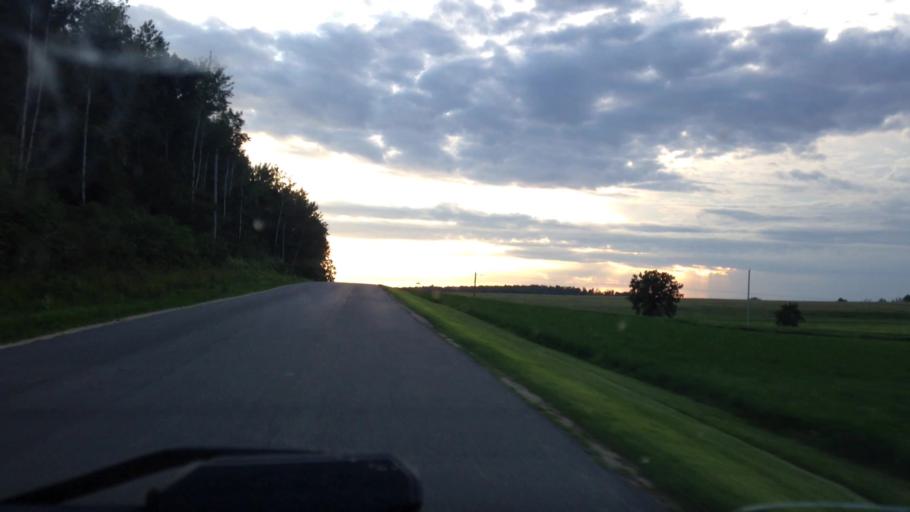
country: US
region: Wisconsin
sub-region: Dodge County
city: Theresa
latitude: 43.4860
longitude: -88.4778
